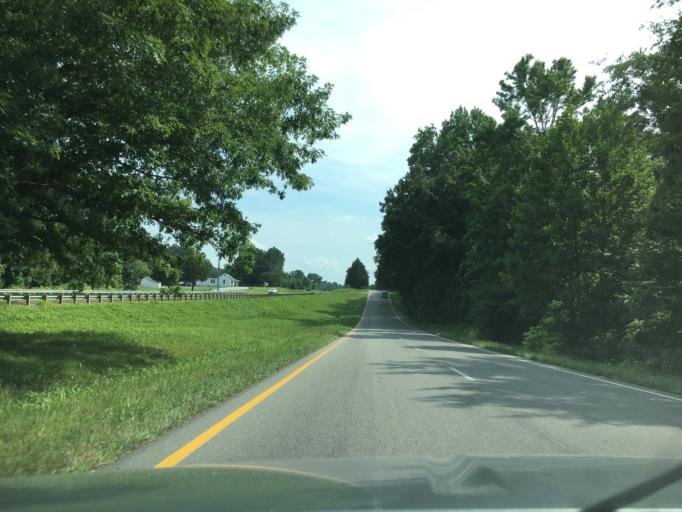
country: US
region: Virginia
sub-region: Nottoway County
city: Crewe
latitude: 37.2446
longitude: -78.1438
